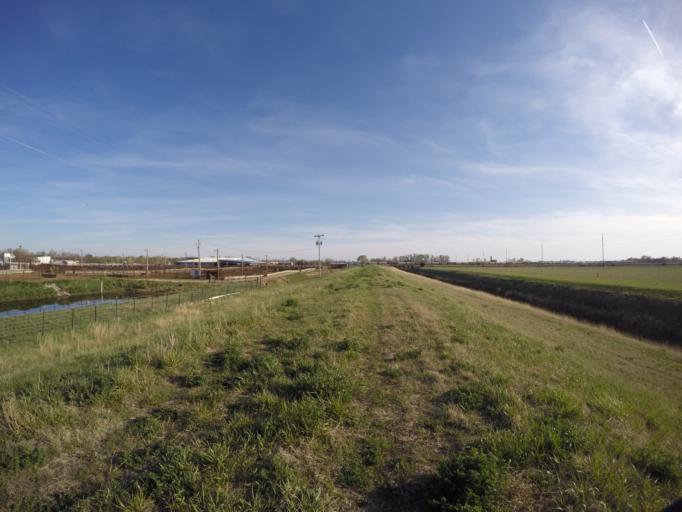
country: US
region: Kansas
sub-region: Saline County
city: Salina
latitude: 38.8480
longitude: -97.6304
